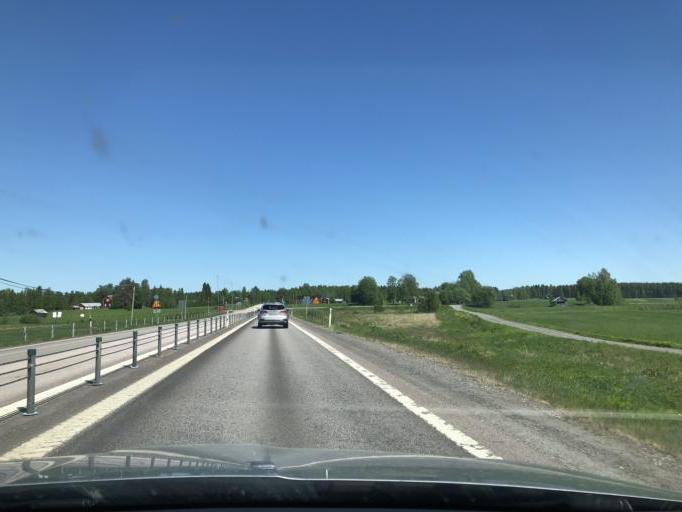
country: SE
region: Norrbotten
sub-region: Lulea Kommun
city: Ranea
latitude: 65.7675
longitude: 22.1680
